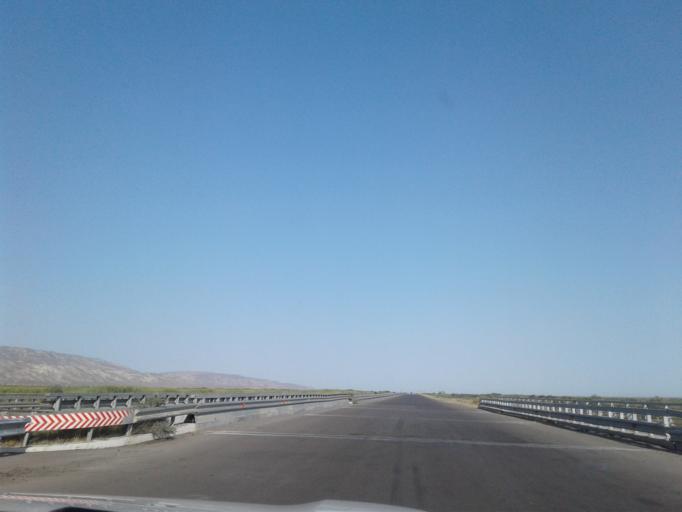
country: TM
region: Balkan
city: Serdar
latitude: 38.8652
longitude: 56.5850
